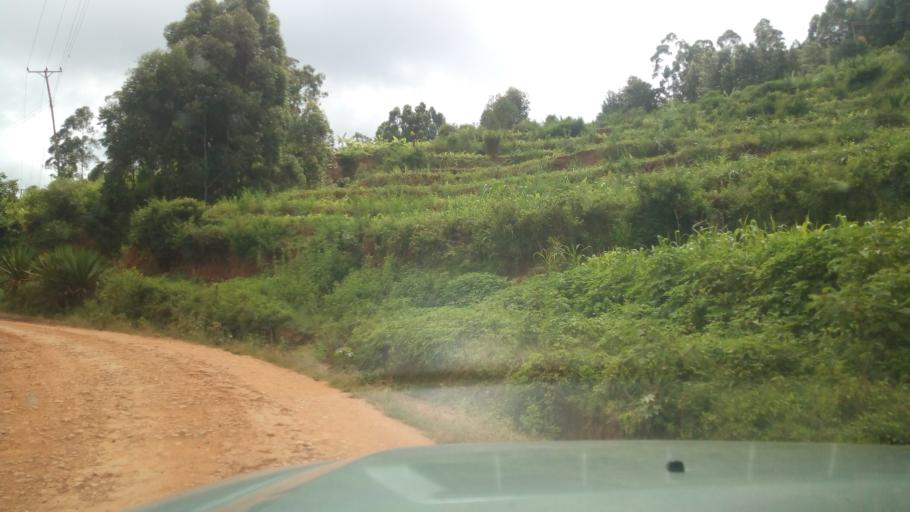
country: KE
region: Makueni
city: Wote
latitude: -1.6723
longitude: 37.4499
